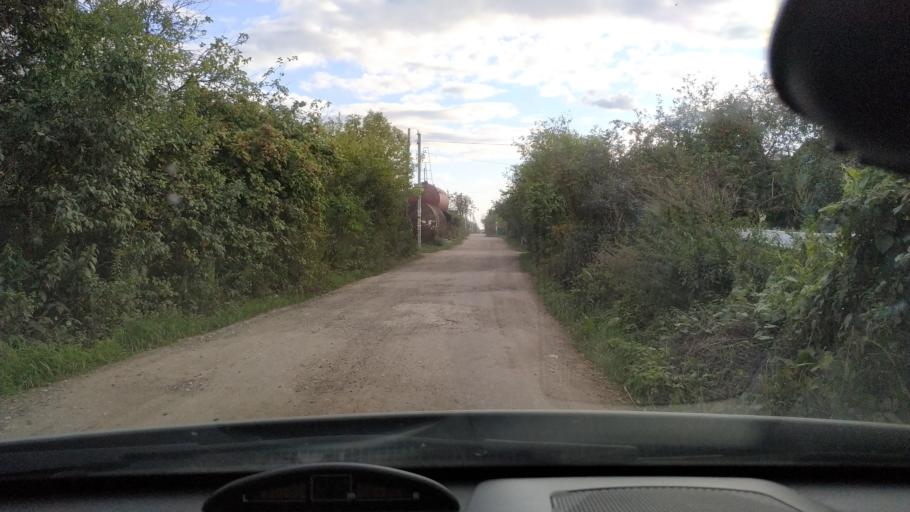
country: RU
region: Rjazan
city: Polyany
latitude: 54.5564
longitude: 39.8749
